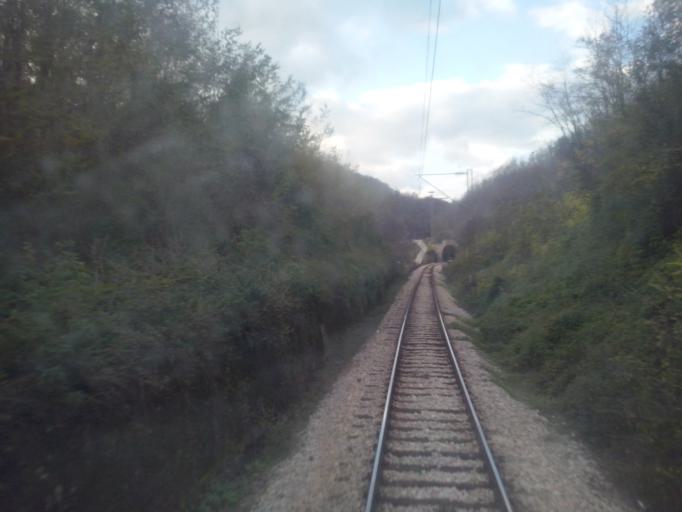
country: RS
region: Central Serbia
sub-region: Zlatiborski Okrug
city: Kosjeric
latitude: 43.9663
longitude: 19.9576
